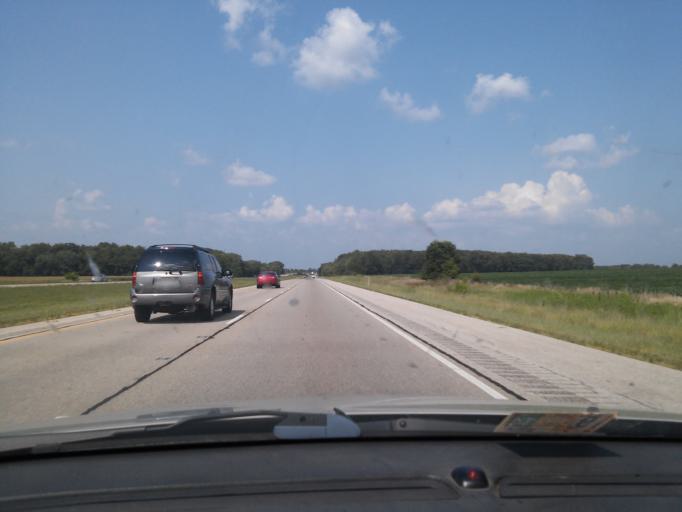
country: US
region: Illinois
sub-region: McLean County
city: Twin Grove
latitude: 40.3670
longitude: -89.1020
